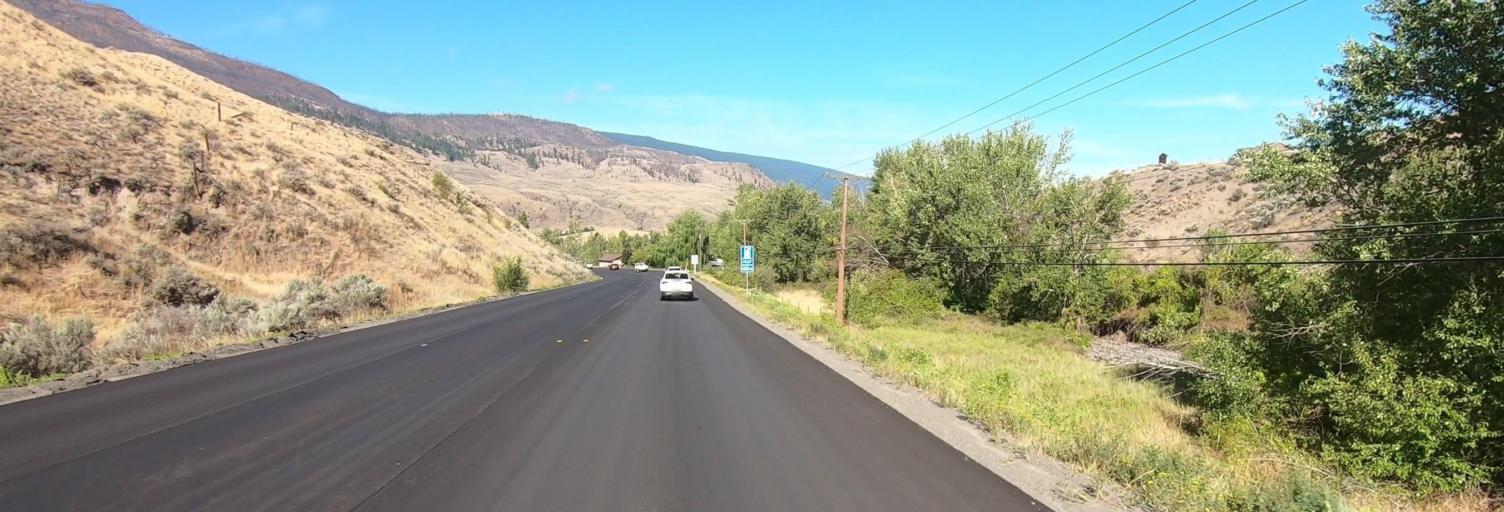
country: CA
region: British Columbia
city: Cache Creek
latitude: 50.8113
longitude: -121.3160
